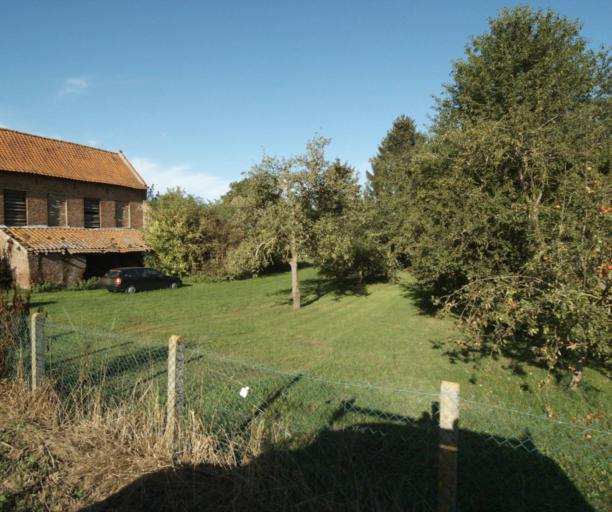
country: FR
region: Nord-Pas-de-Calais
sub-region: Departement du Nord
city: Gruson
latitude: 50.5822
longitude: 3.1924
